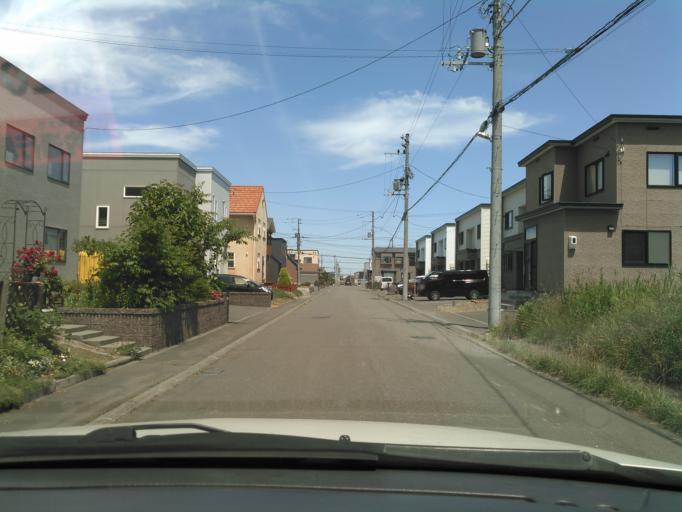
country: JP
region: Hokkaido
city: Ebetsu
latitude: 43.0959
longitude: 141.5680
